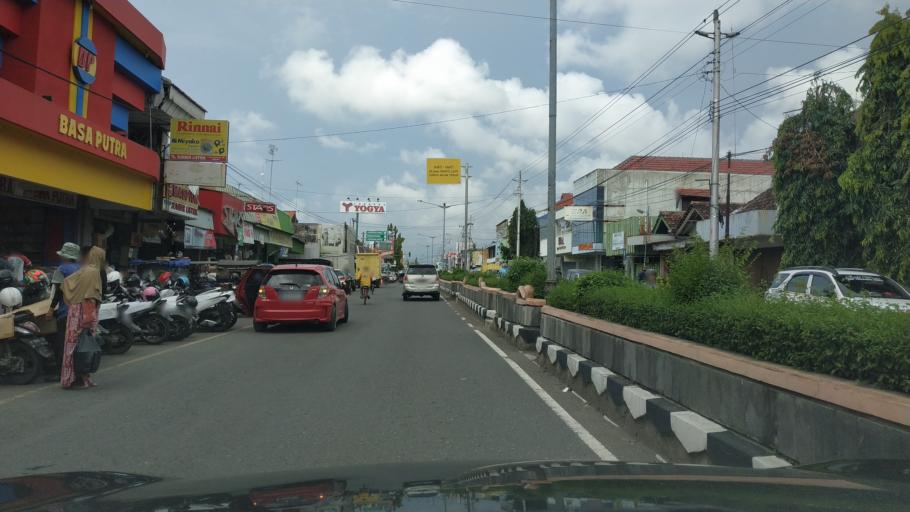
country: ID
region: Central Java
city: Pemalang
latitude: -6.8902
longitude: 109.3871
